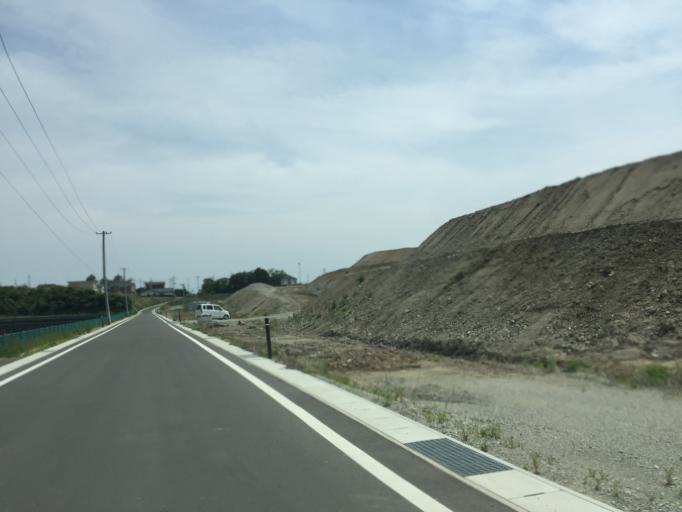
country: JP
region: Miyagi
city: Marumori
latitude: 37.8290
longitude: 140.9545
